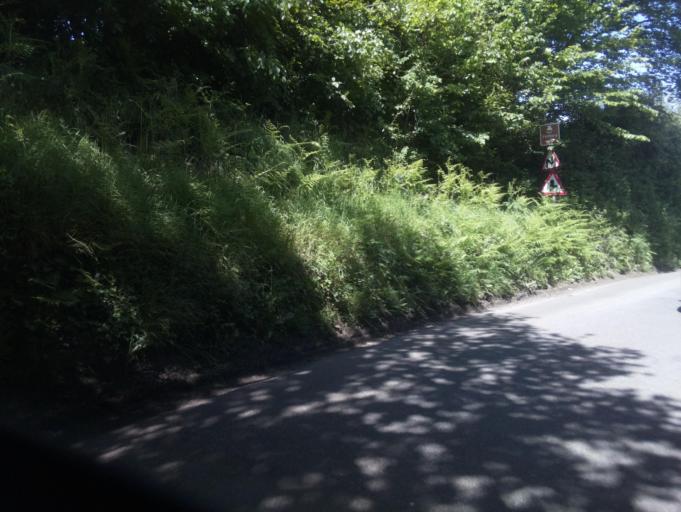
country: GB
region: England
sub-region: Devon
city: Ottery St Mary
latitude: 50.7346
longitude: -3.2766
